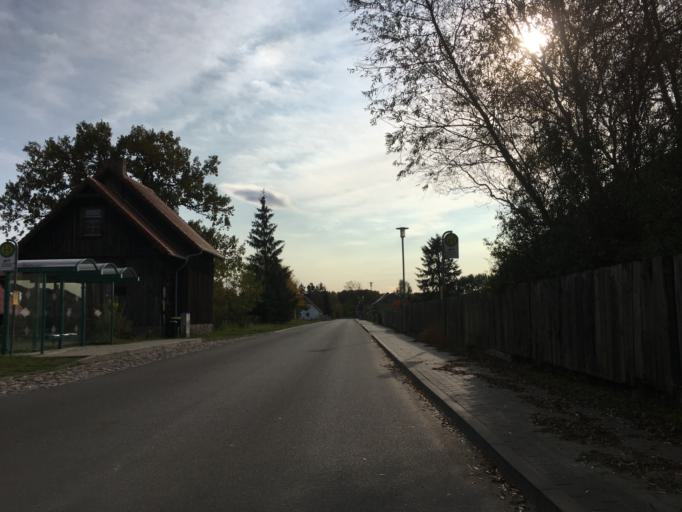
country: DE
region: Brandenburg
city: Templin
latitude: 53.0243
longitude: 13.4797
